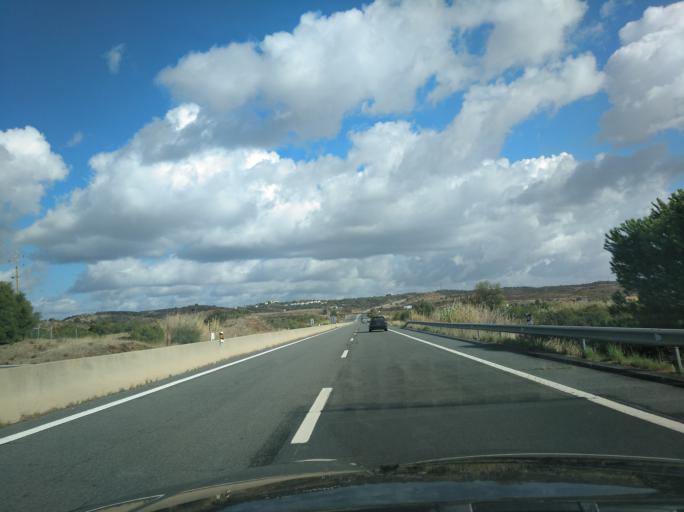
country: PT
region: Faro
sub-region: Castro Marim
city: Castro Marim
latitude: 37.2168
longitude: -7.4812
